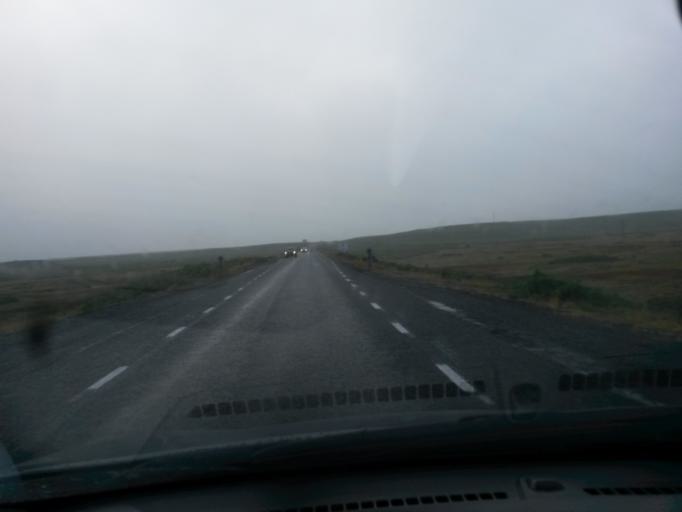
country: IS
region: South
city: Vestmannaeyjar
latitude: 63.4990
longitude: -19.4026
